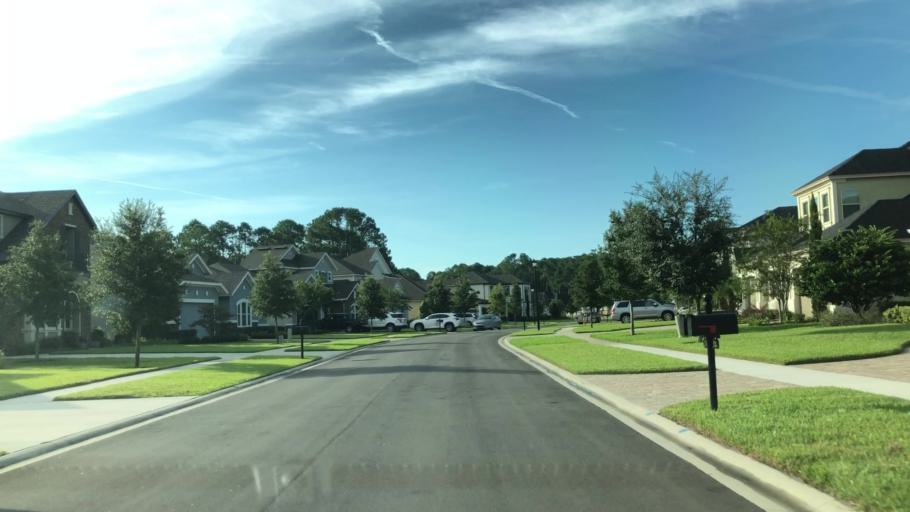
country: US
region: Florida
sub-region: Saint Johns County
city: Palm Valley
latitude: 30.1328
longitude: -81.4282
